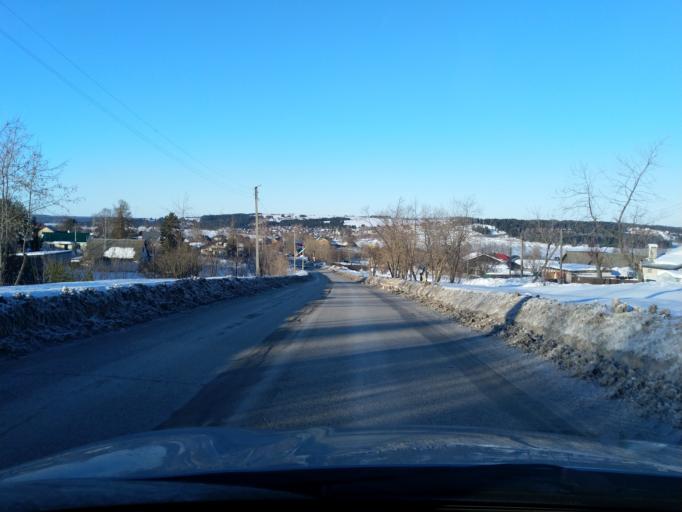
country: RU
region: Perm
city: Polazna
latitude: 58.2931
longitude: 56.4154
